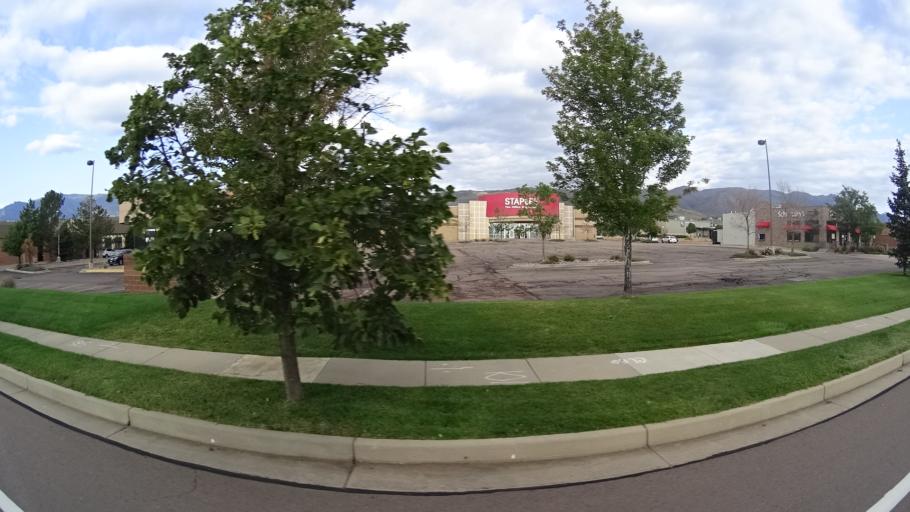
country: US
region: Colorado
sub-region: El Paso County
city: Colorado Springs
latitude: 38.8978
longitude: -104.8511
